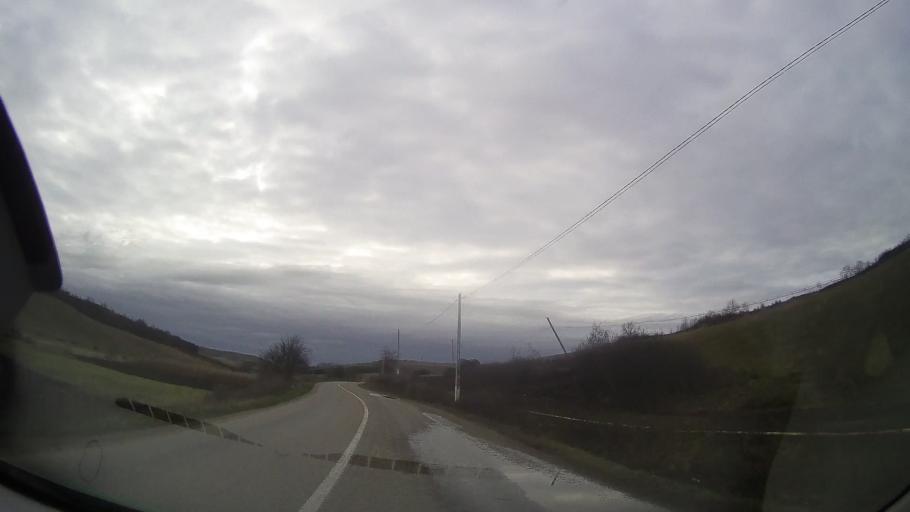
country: RO
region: Bistrita-Nasaud
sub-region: Comuna Budesti
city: Budesti
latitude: 46.8637
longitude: 24.2447
